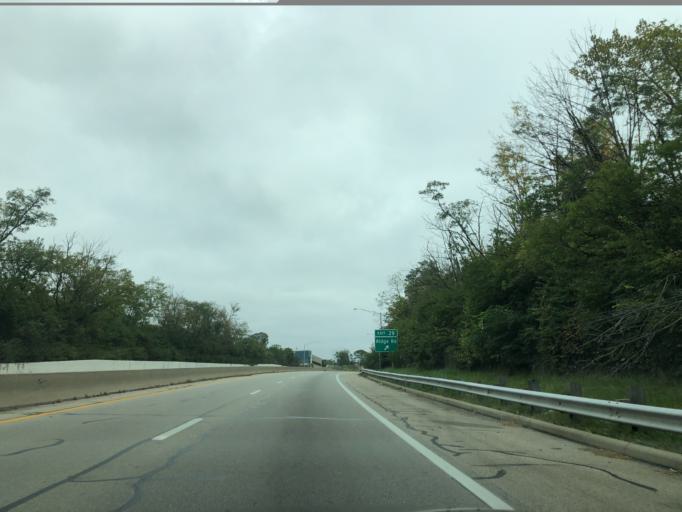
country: US
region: Ohio
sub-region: Hamilton County
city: Amberley
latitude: 39.2160
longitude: -84.4327
